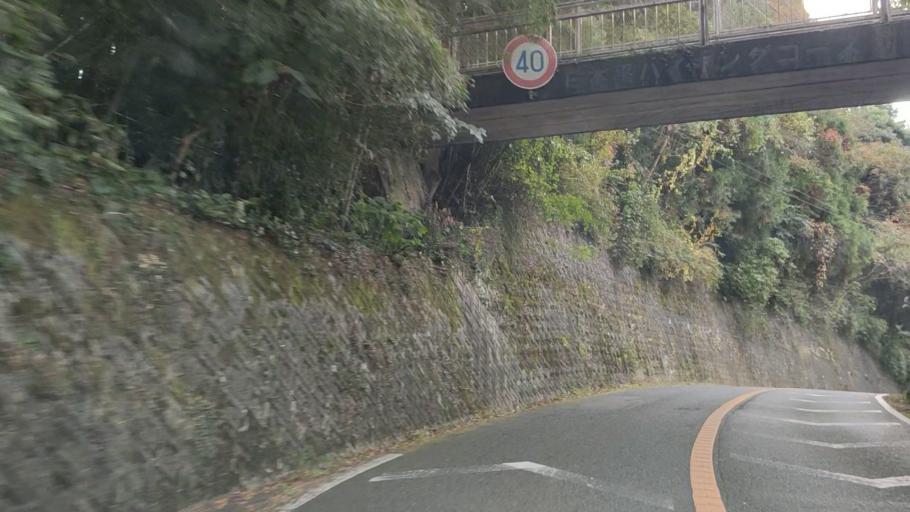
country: JP
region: Shizuoka
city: Shizuoka-shi
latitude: 34.9901
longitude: 138.4607
